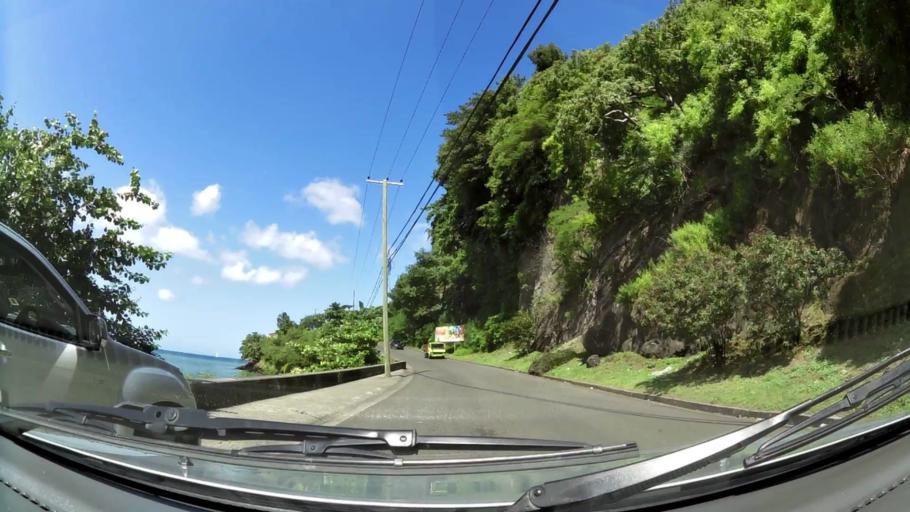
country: GD
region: Saint George
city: Saint George's
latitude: 12.0613
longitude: -61.7550
